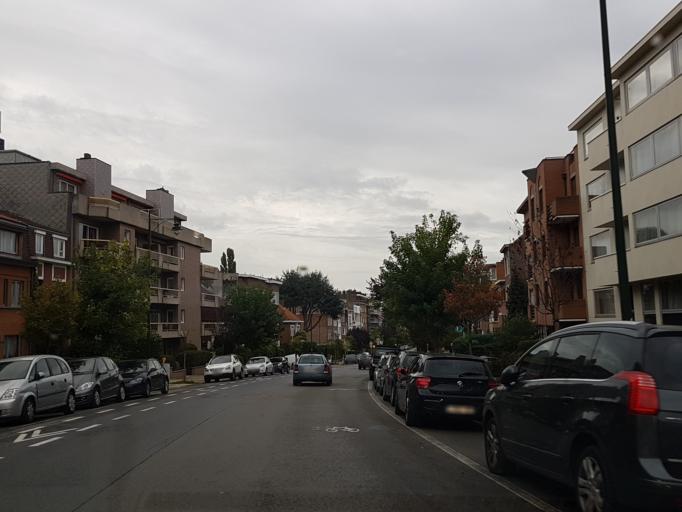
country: BE
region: Brussels Capital
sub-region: Bruxelles-Capitale
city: Brussels
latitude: 50.8187
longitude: 4.4095
